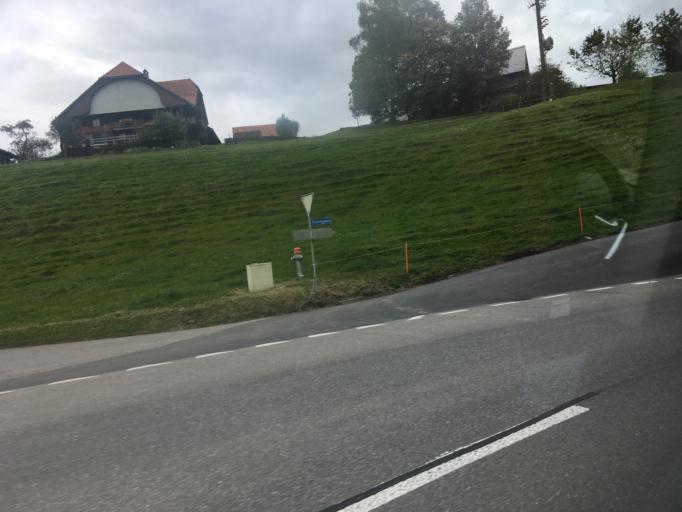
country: CH
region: Bern
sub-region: Bern-Mittelland District
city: Ruschegg
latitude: 46.8094
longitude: 7.3817
